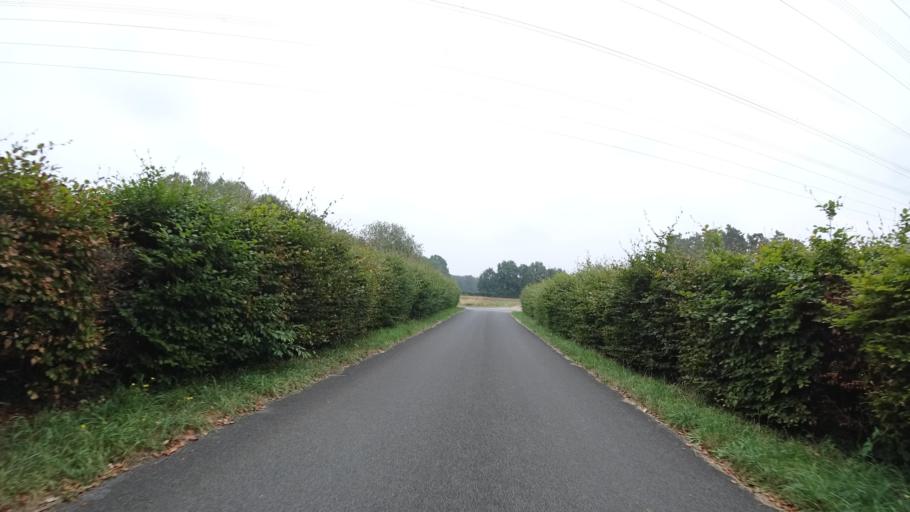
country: DE
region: North Rhine-Westphalia
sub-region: Regierungsbezirk Detmold
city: Guetersloh
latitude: 51.9103
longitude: 8.3342
